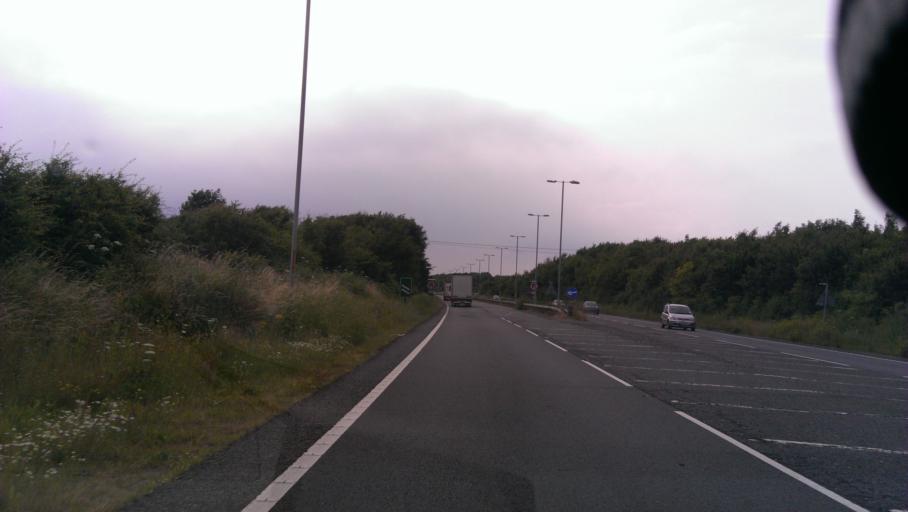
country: GB
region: England
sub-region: Kent
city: Dover
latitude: 51.1510
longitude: 1.3180
